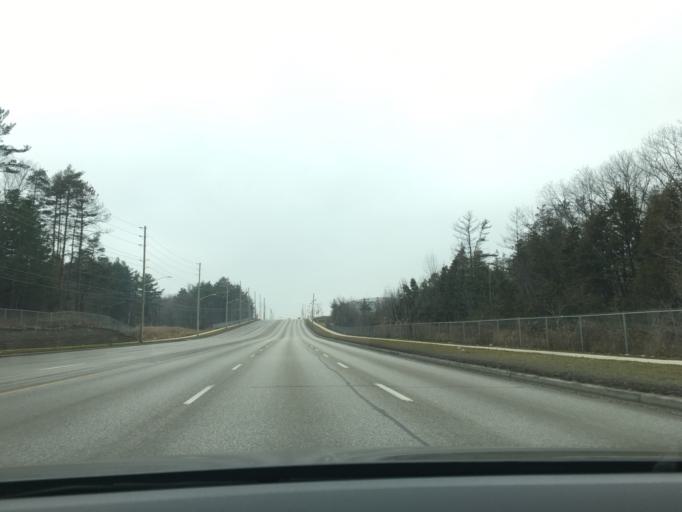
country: CA
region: Ontario
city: Innisfil
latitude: 44.3385
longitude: -79.6718
